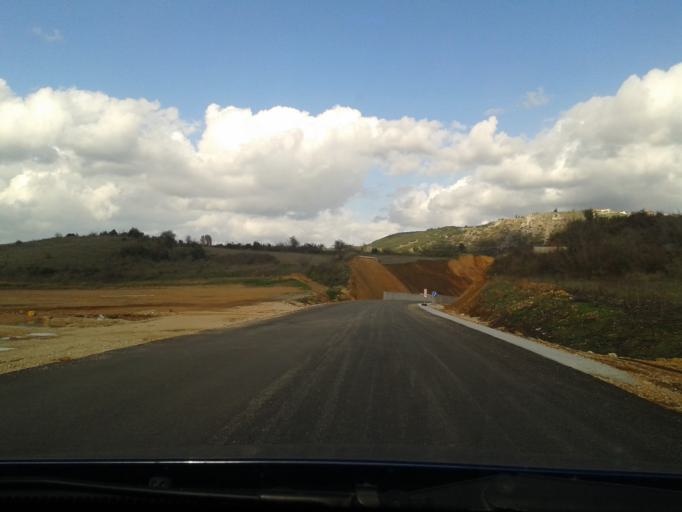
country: GR
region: West Greece
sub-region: Nomos Aitolias kai Akarnanias
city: Fitiai
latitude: 38.6851
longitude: 21.1690
